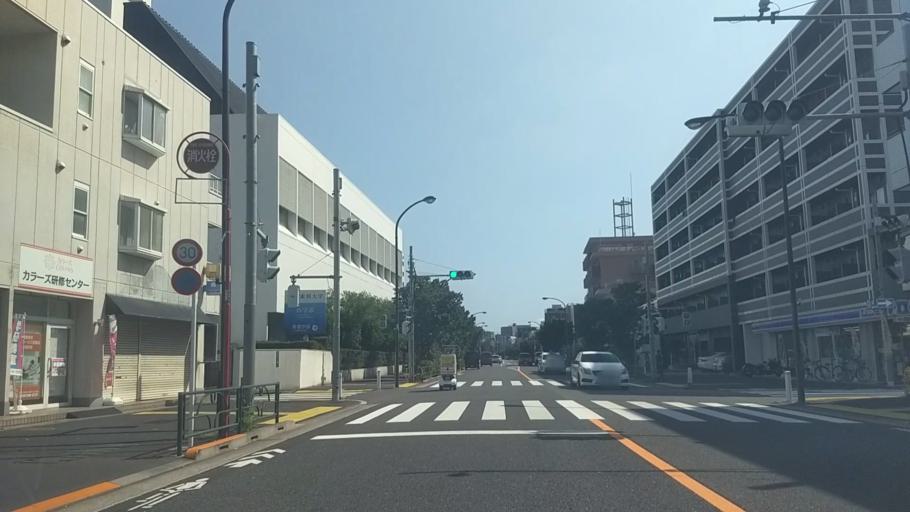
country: JP
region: Kanagawa
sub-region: Kawasaki-shi
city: Kawasaki
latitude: 35.5718
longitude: 139.7243
